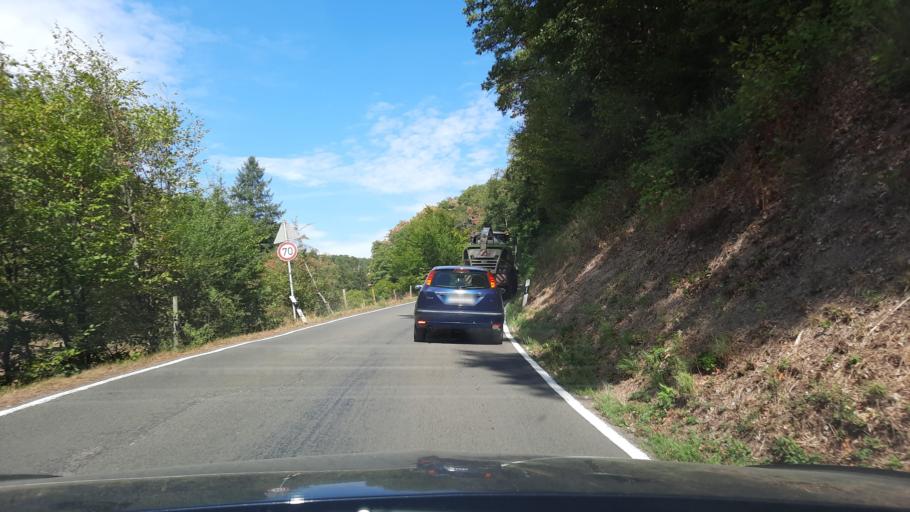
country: DE
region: Rheinland-Pfalz
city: Saarburg
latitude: 49.6171
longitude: 6.5331
